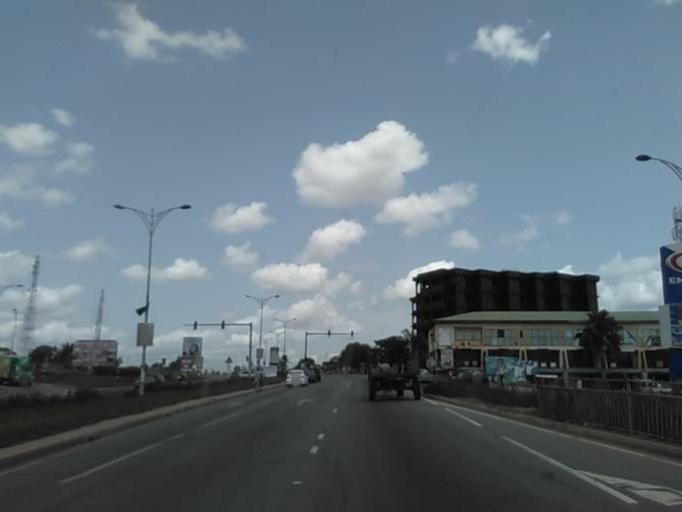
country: GH
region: Ashanti
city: Kumasi
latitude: 6.6686
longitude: -1.6061
